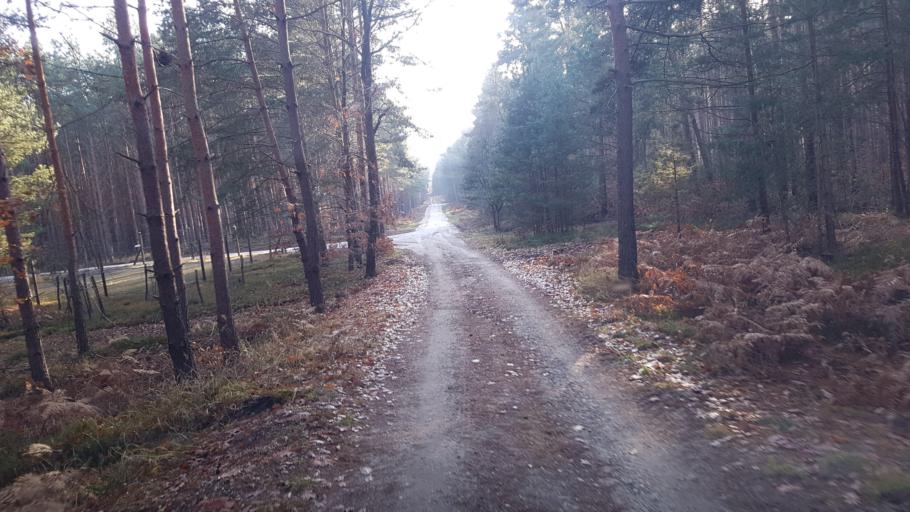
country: DE
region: Brandenburg
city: Plessa
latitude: 51.5263
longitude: 13.6714
